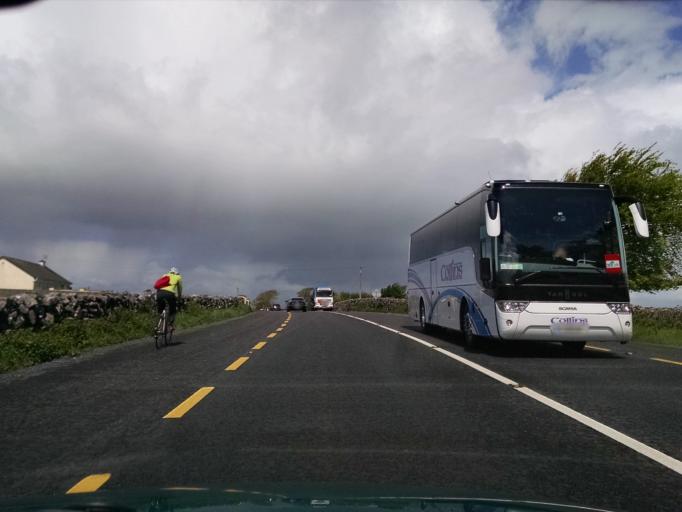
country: IE
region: Connaught
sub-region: County Galway
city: Oranmore
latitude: 53.2374
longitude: -8.8836
